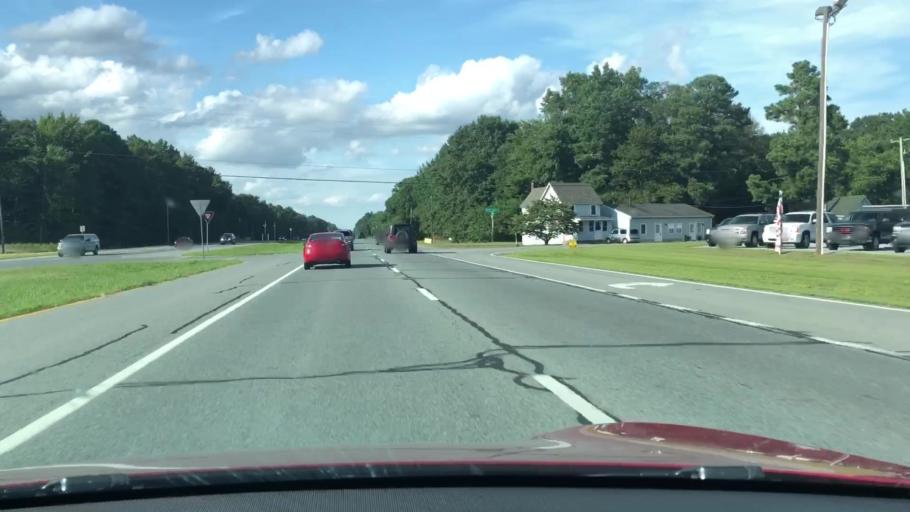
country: US
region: Delaware
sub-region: Kent County
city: Woodside East
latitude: 39.0576
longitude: -75.5554
